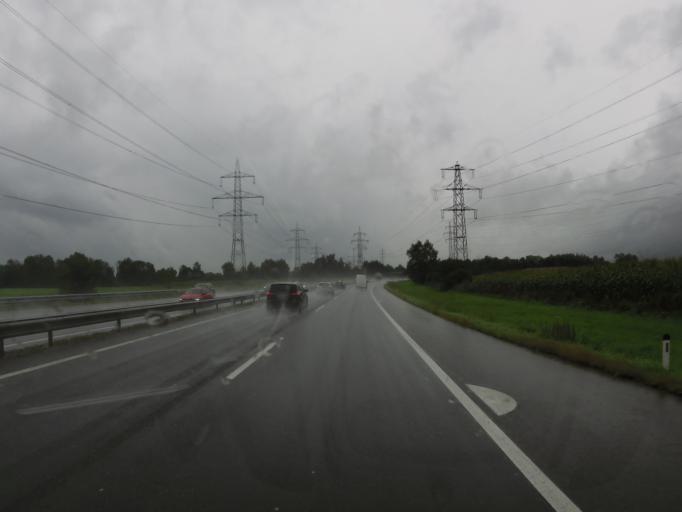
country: AT
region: Vorarlberg
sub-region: Politischer Bezirk Dornbirn
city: Hohenems
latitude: 47.3877
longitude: 9.6790
